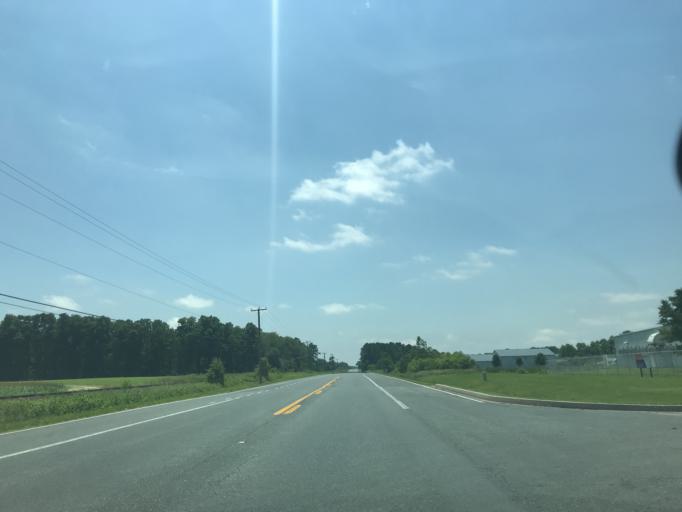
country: US
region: Maryland
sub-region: Dorchester County
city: Hurlock
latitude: 38.6233
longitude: -75.8791
